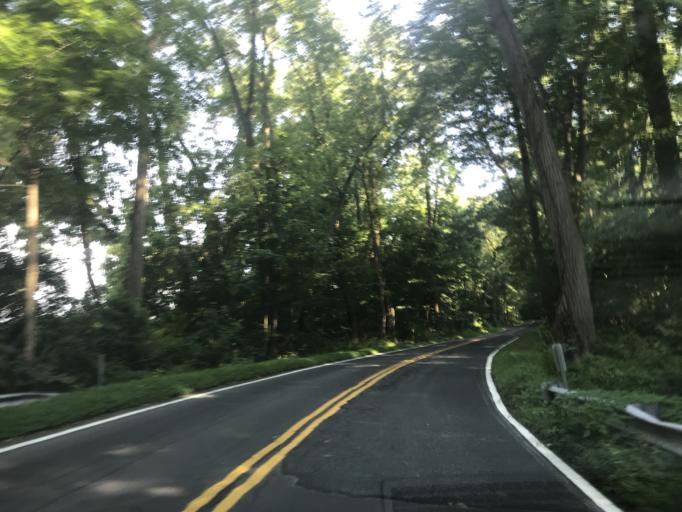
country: US
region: Maryland
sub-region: Harford County
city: Aberdeen
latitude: 39.5179
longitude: -76.1243
